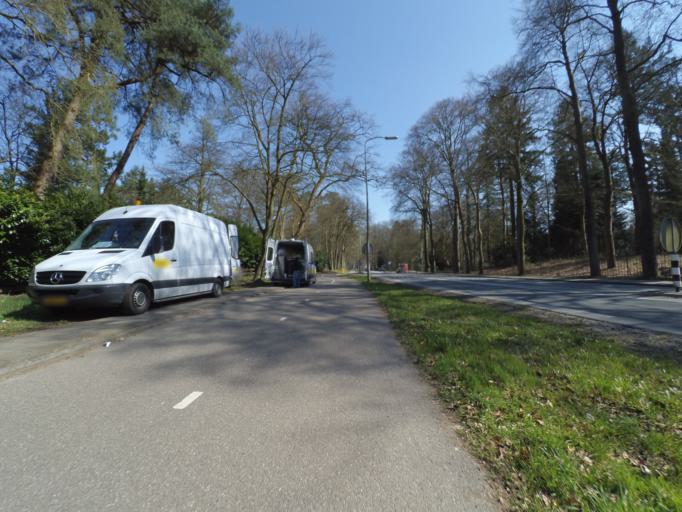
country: NL
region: Utrecht
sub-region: Gemeente Utrechtse Heuvelrug
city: Doorn
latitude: 52.0357
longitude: 5.3281
